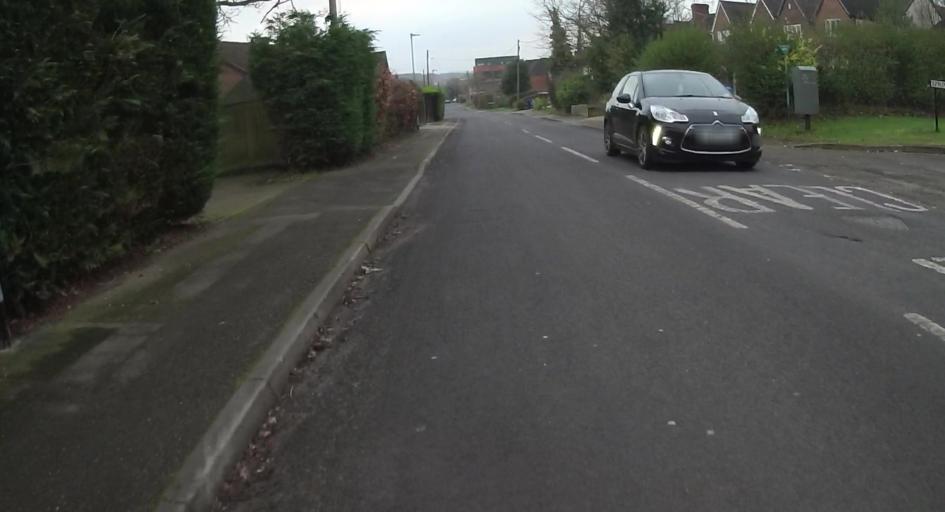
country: GB
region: England
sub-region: Bracknell Forest
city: Binfield
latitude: 51.4184
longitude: -0.7858
